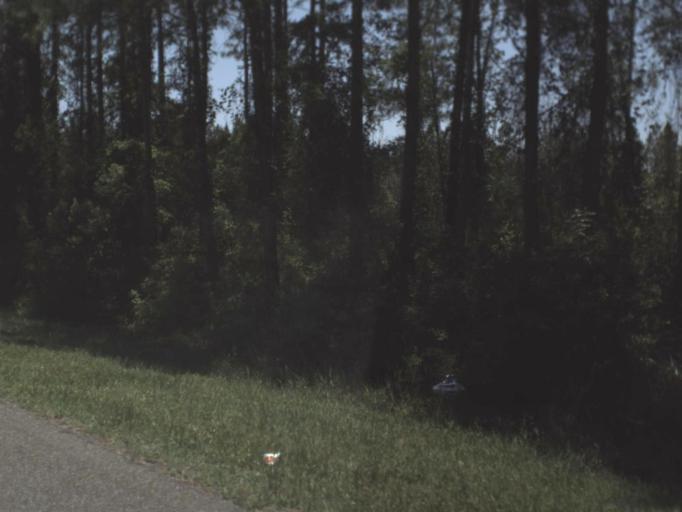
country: US
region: Florida
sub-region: Suwannee County
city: Wellborn
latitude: 30.2152
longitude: -82.8160
